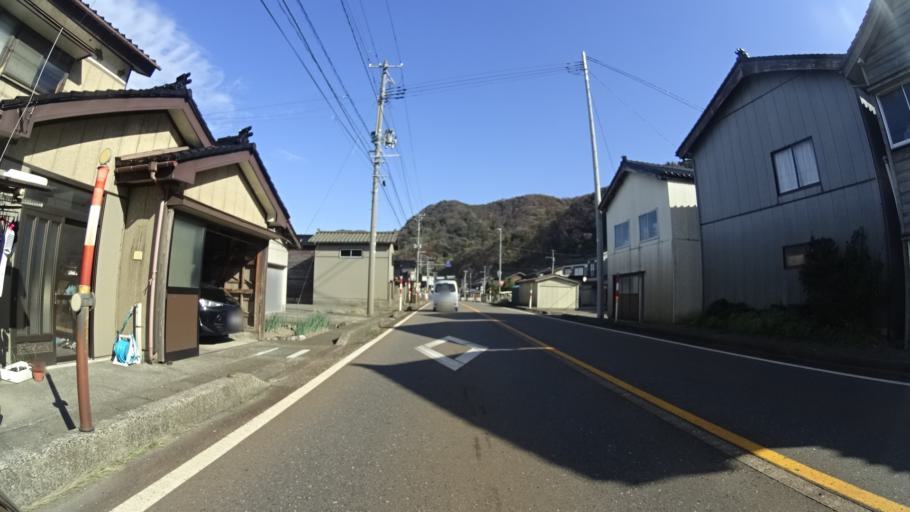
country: JP
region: Niigata
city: Itoigawa
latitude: 37.0728
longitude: 137.9359
